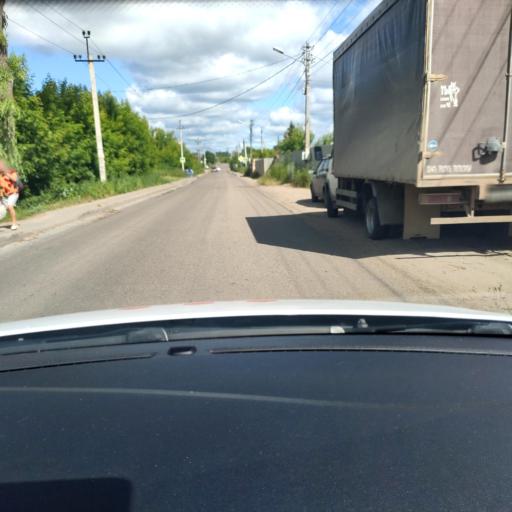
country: RU
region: Tatarstan
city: Vysokaya Gora
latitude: 55.8603
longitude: 49.2402
